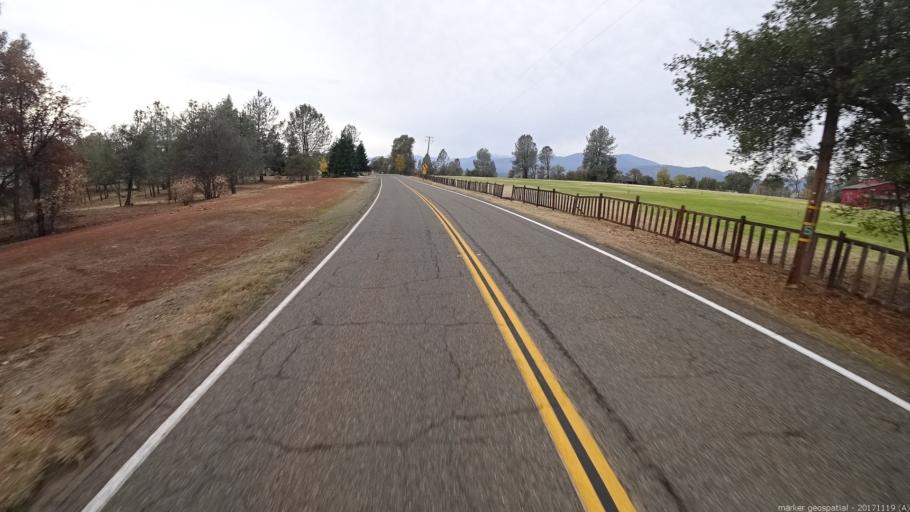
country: US
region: California
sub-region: Shasta County
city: Redding
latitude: 40.4881
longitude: -122.4431
